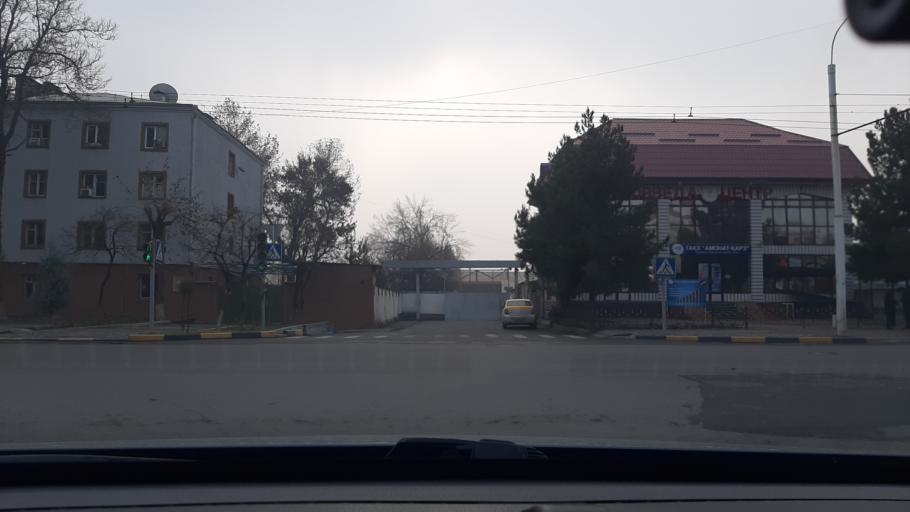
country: TJ
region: Dushanbe
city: Dushanbe
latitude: 38.5581
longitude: 68.7952
